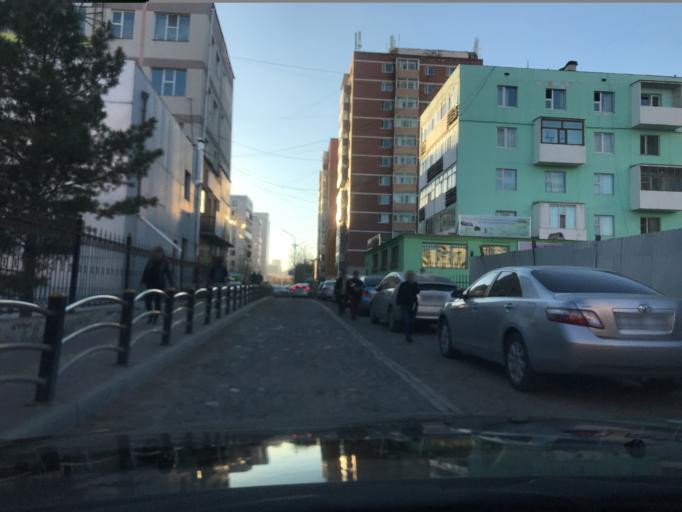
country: MN
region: Ulaanbaatar
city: Ulaanbaatar
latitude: 47.9235
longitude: 106.9049
